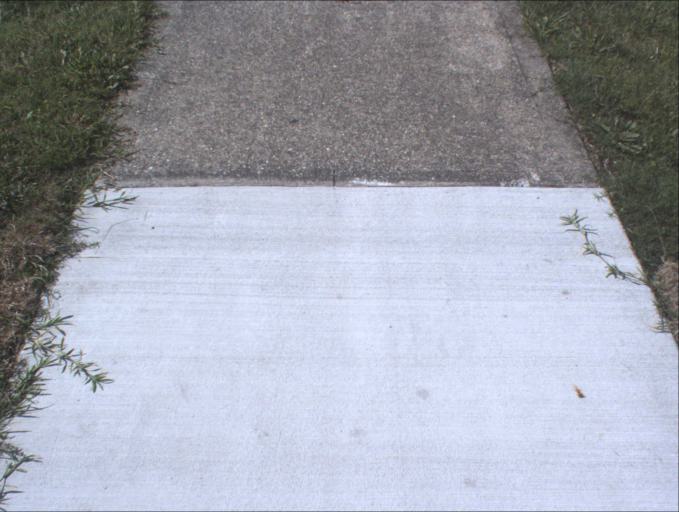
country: AU
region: Queensland
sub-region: Logan
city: Waterford West
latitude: -27.6968
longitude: 153.1582
